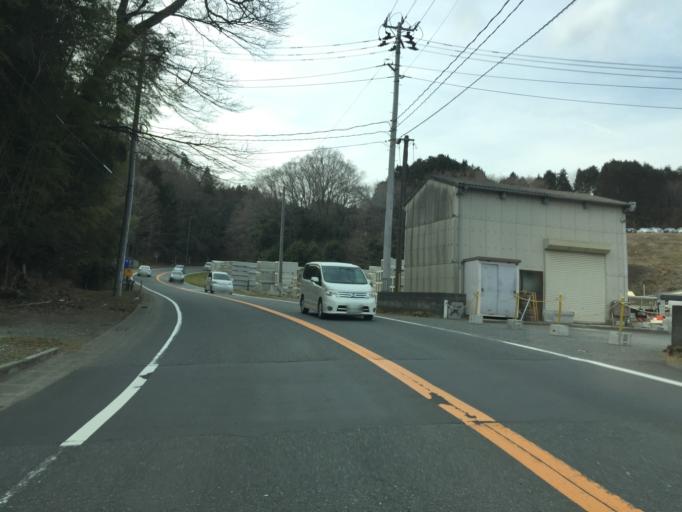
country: JP
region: Fukushima
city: Iwaki
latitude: 36.9715
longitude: 140.7421
